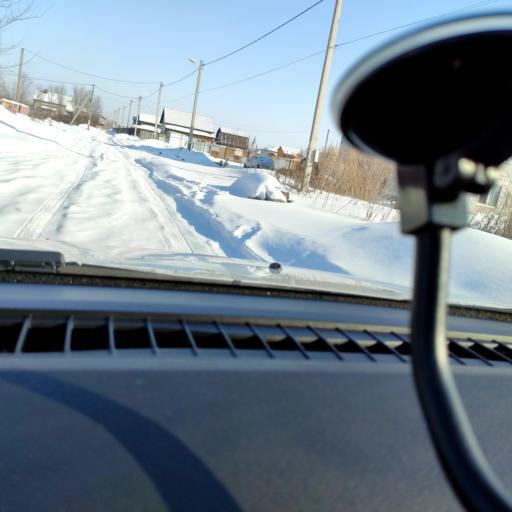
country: RU
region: Samara
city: Samara
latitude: 53.1353
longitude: 50.2517
